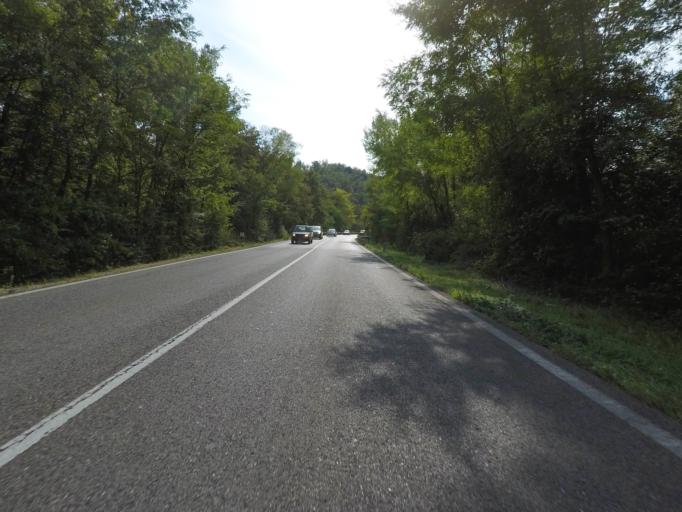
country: IT
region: Tuscany
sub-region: Provincia di Siena
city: Rosia
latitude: 43.1927
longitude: 11.2776
